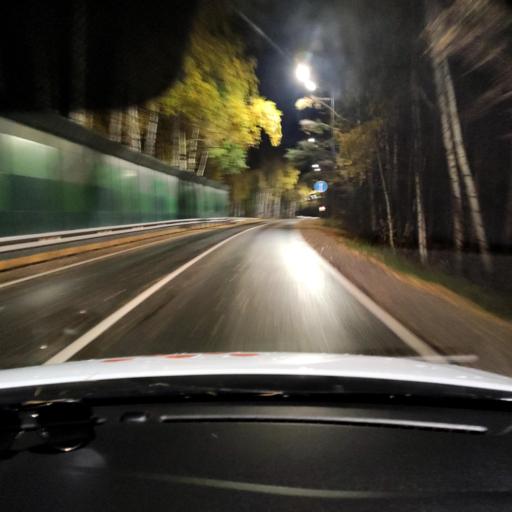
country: RU
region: Tatarstan
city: Verkhniy Uslon
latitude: 55.6290
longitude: 49.0145
